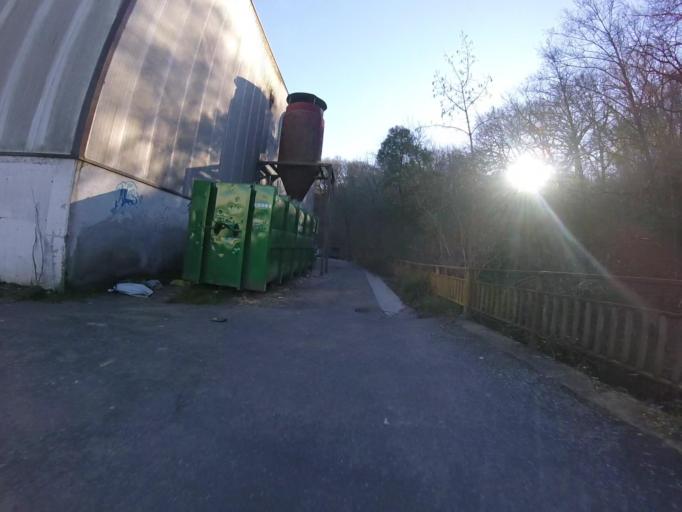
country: ES
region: Basque Country
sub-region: Provincia de Guipuzcoa
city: Errenteria
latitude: 43.2998
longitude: -1.8846
